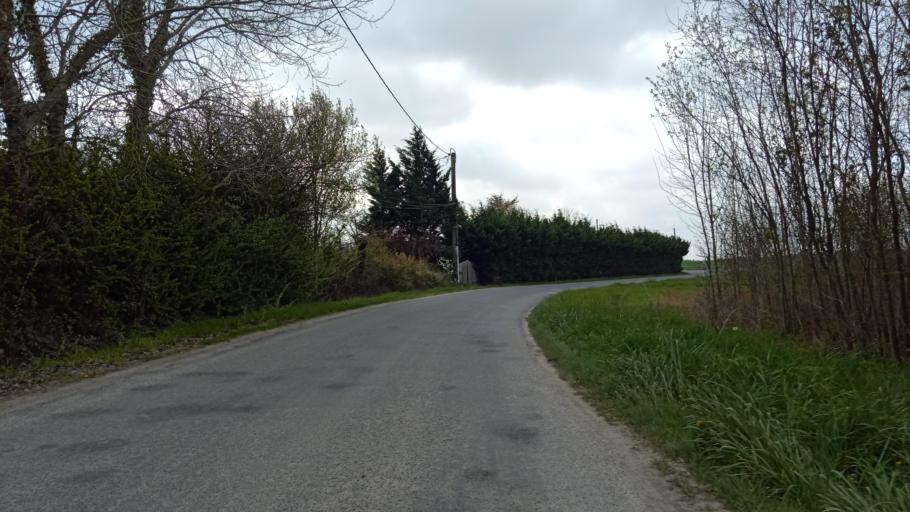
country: FR
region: Poitou-Charentes
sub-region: Departement de la Charente-Maritime
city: Verines
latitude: 46.1526
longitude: -0.9324
